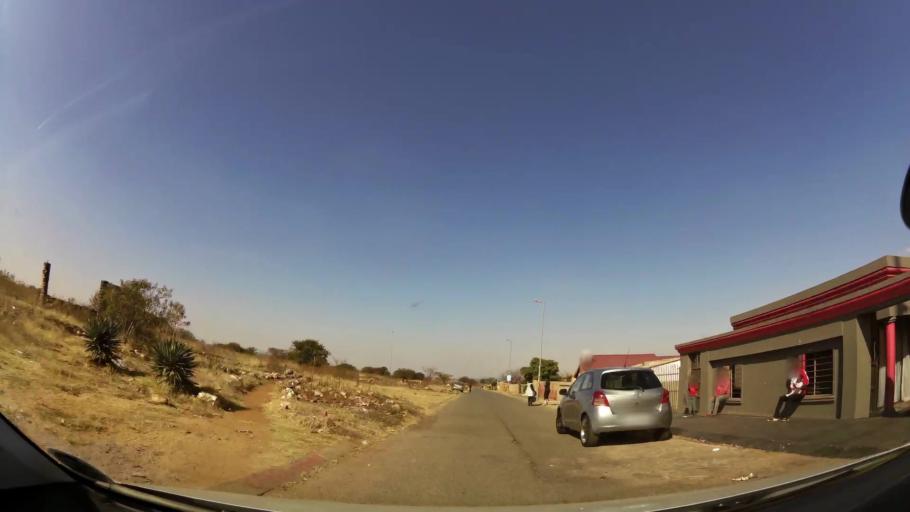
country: ZA
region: Gauteng
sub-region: City of Johannesburg Metropolitan Municipality
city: Soweto
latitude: -26.2818
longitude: 27.8690
